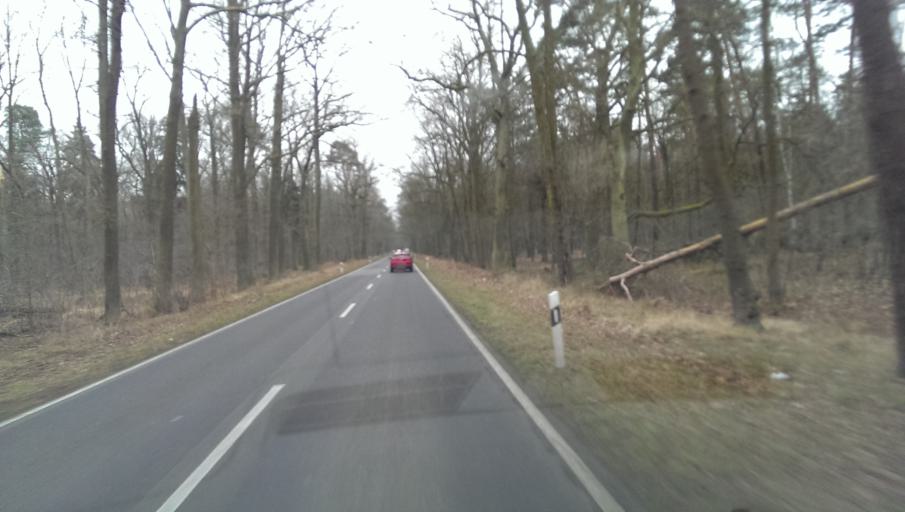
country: DE
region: Brandenburg
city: Grossbeeren
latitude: 52.3364
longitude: 13.3002
